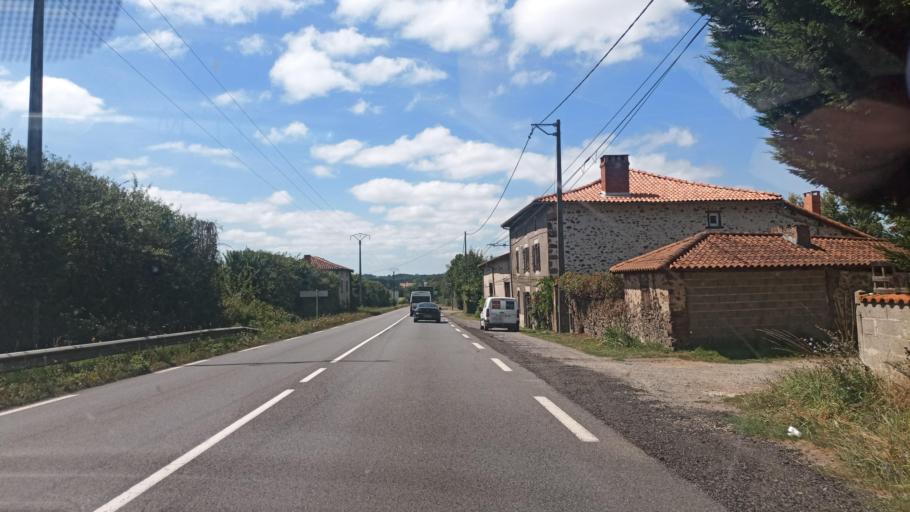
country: FR
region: Poitou-Charentes
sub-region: Departement de la Charente
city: Exideuil
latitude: 45.8721
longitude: 0.6861
